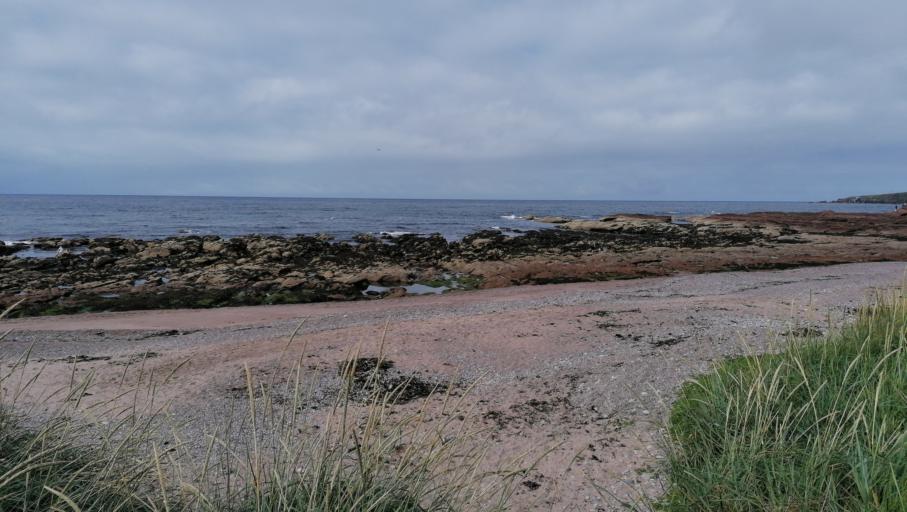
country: GB
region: Scotland
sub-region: Aberdeenshire
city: Rosehearty
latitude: 57.6712
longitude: -2.1907
